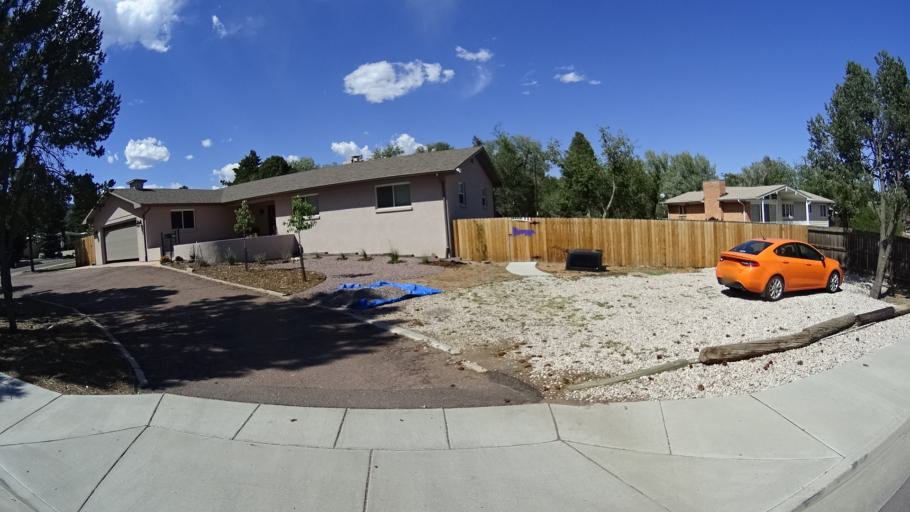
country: US
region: Colorado
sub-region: El Paso County
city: Colorado Springs
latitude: 38.8127
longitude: -104.8580
